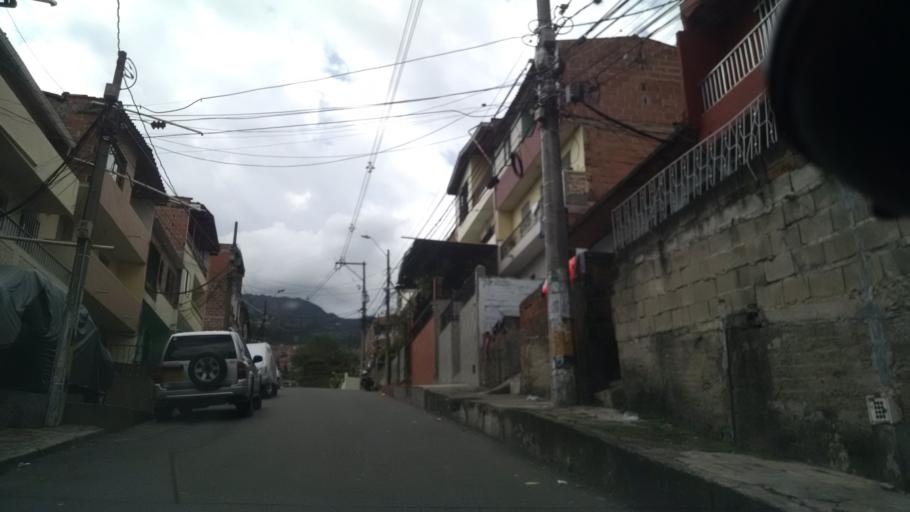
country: CO
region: Antioquia
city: Bello
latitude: 6.3005
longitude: -75.5734
